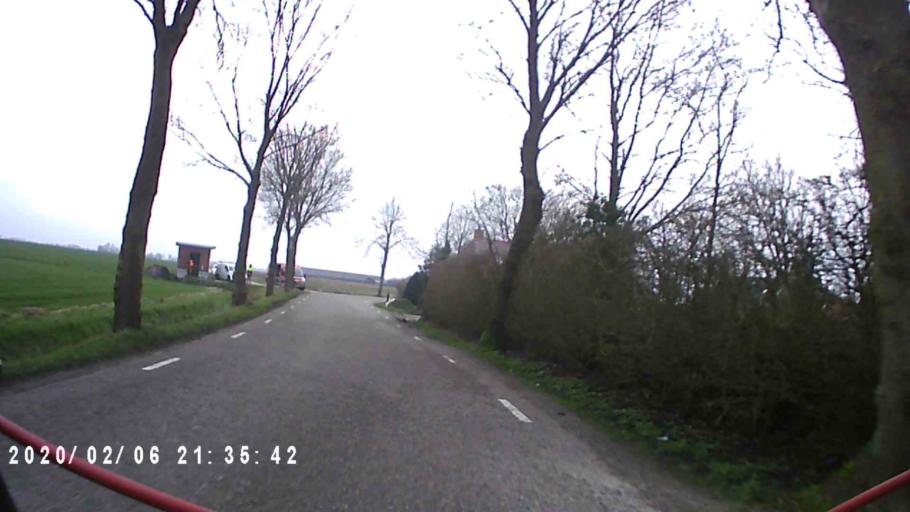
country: NL
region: Groningen
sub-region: Gemeente Zuidhorn
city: Noordhorn
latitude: 53.2695
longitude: 6.3930
